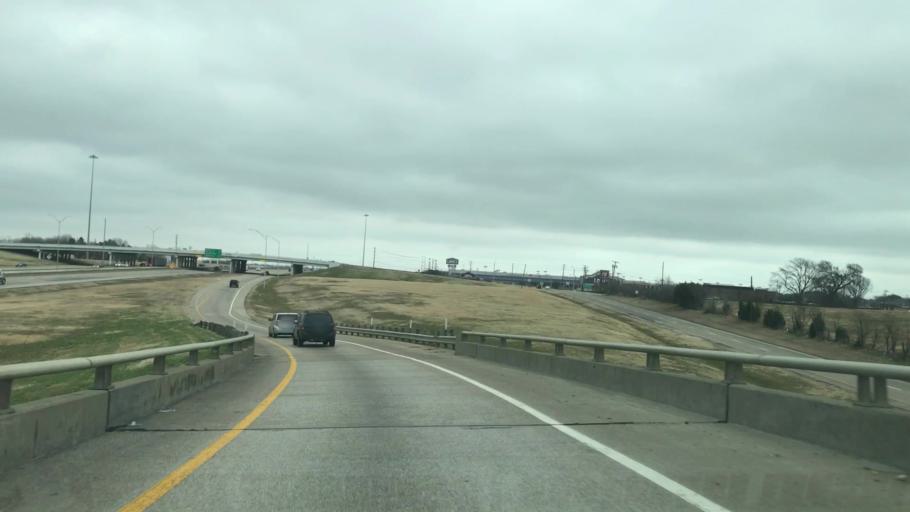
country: US
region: Texas
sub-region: Dallas County
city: Mesquite
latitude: 32.8234
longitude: -96.6274
